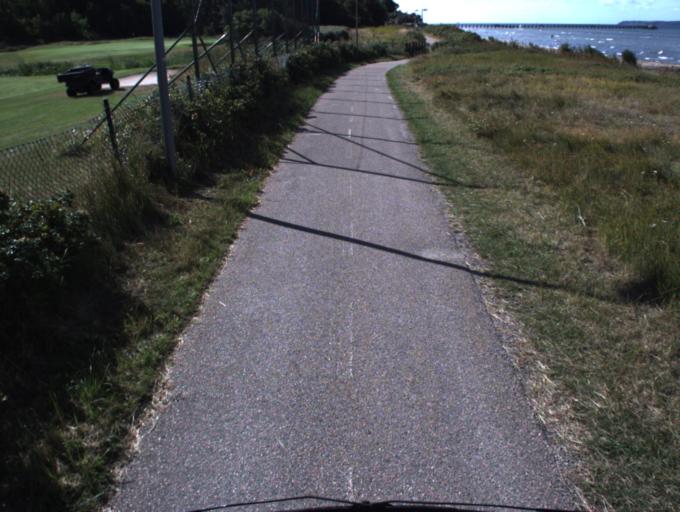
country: SE
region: Skane
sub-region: Helsingborg
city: Rydeback
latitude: 55.9718
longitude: 12.7568
